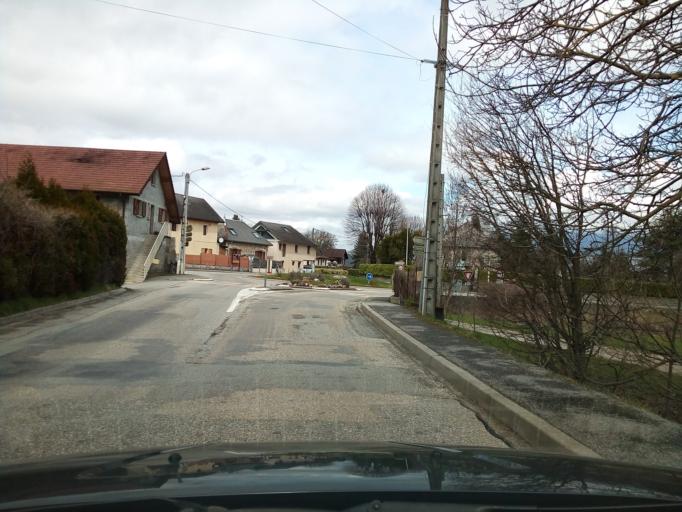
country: FR
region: Rhone-Alpes
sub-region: Departement de la Savoie
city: Saint-Baldoph
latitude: 45.5124
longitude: 5.9588
